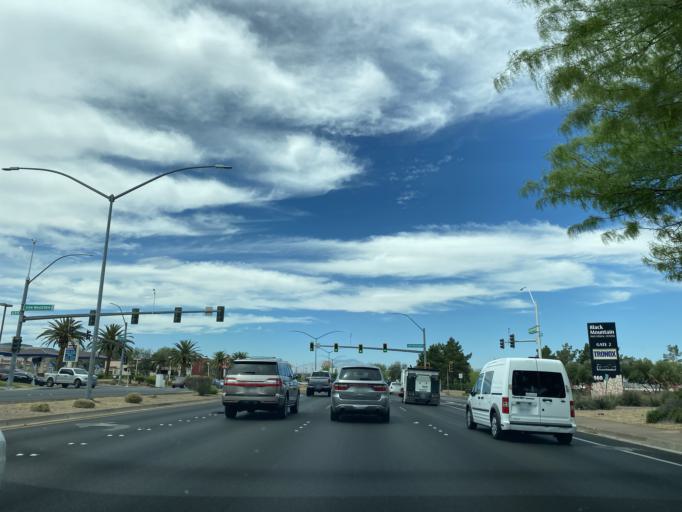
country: US
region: Nevada
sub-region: Clark County
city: Henderson
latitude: 36.0355
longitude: -114.9996
